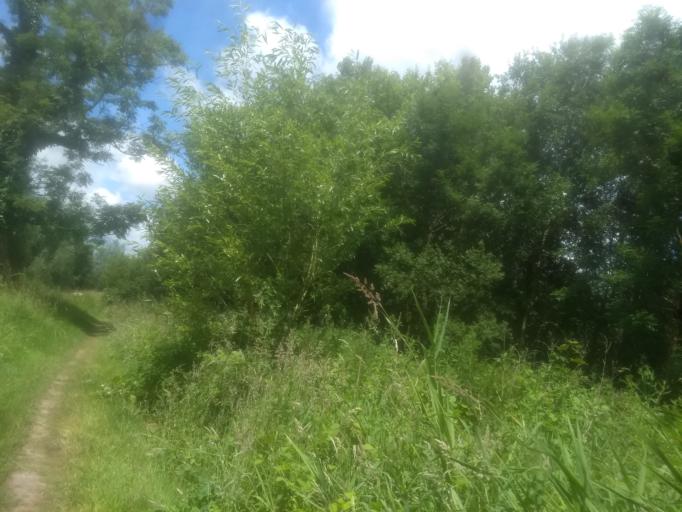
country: FR
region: Nord-Pas-de-Calais
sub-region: Departement du Pas-de-Calais
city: Maroeuil
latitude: 50.3163
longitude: 2.7087
